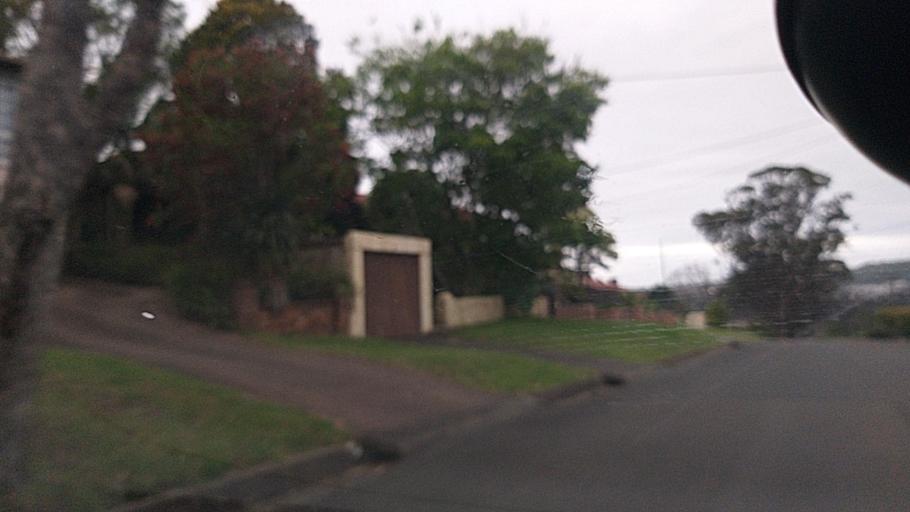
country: AU
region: New South Wales
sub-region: Wollongong
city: Mount Saint Thomas
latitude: -34.4411
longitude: 150.8711
